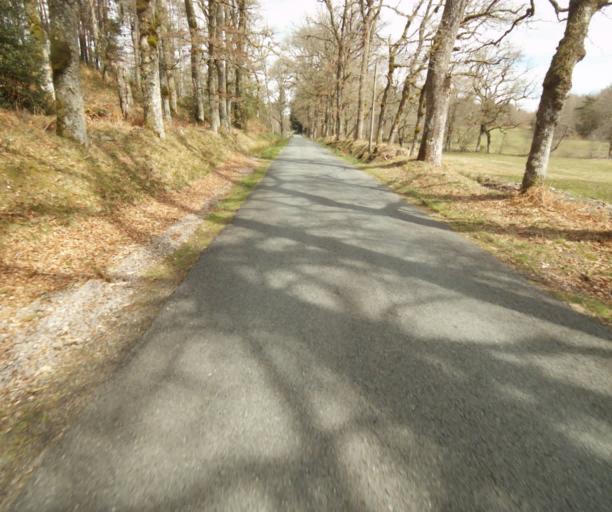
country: FR
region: Limousin
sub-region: Departement de la Correze
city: Correze
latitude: 45.3801
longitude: 1.9537
